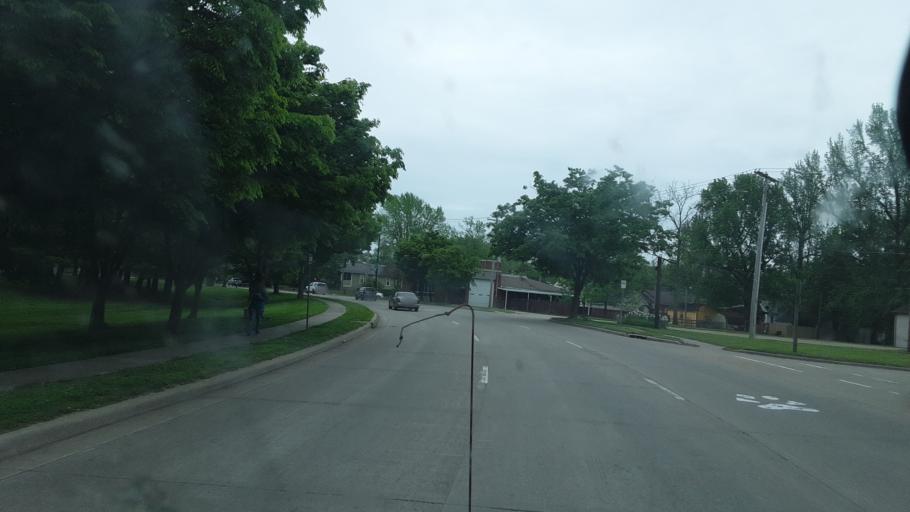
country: US
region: Illinois
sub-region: Jackson County
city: Carbondale
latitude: 37.7246
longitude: -89.2294
